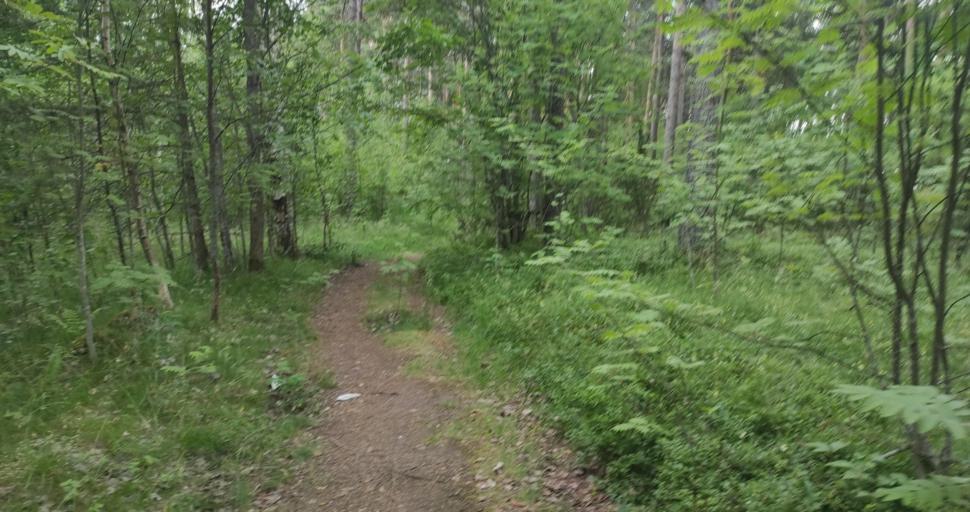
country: RU
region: Leningrad
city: Sosnovyy Bor
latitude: 60.1629
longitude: 29.1445
